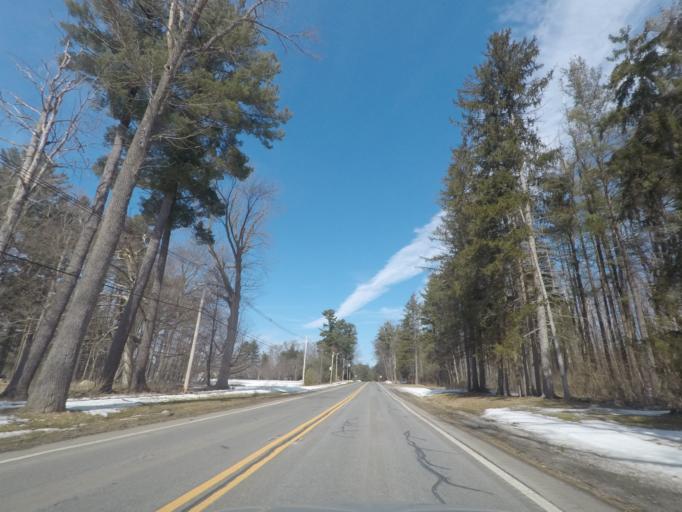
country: US
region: Massachusetts
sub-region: Berkshire County
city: Lenox
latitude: 42.3456
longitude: -73.2820
